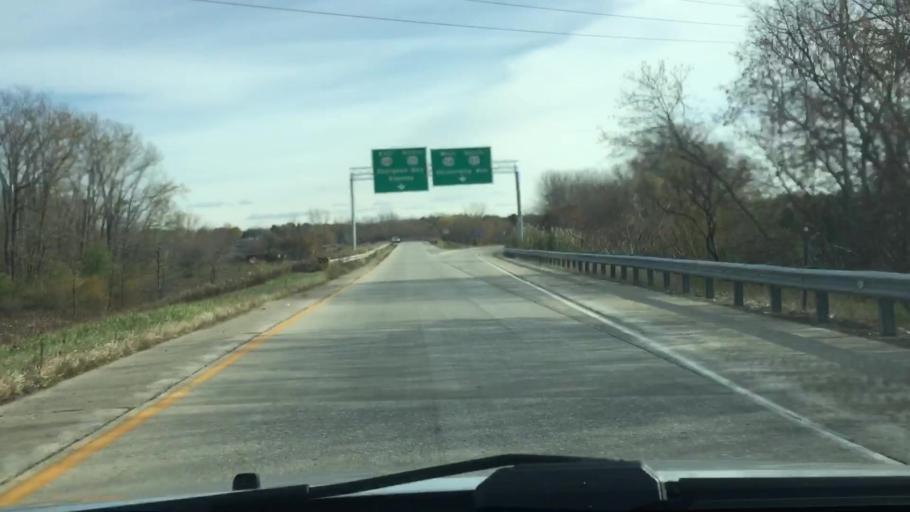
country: US
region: Wisconsin
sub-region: Brown County
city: Green Bay
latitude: 44.5187
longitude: -87.9616
